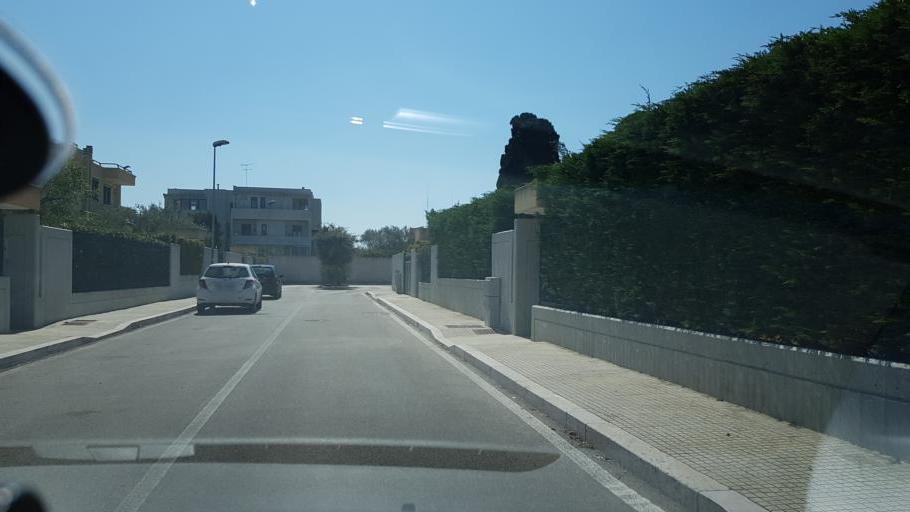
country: IT
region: Apulia
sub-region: Provincia di Brindisi
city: Brindisi
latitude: 40.6469
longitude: 17.9336
